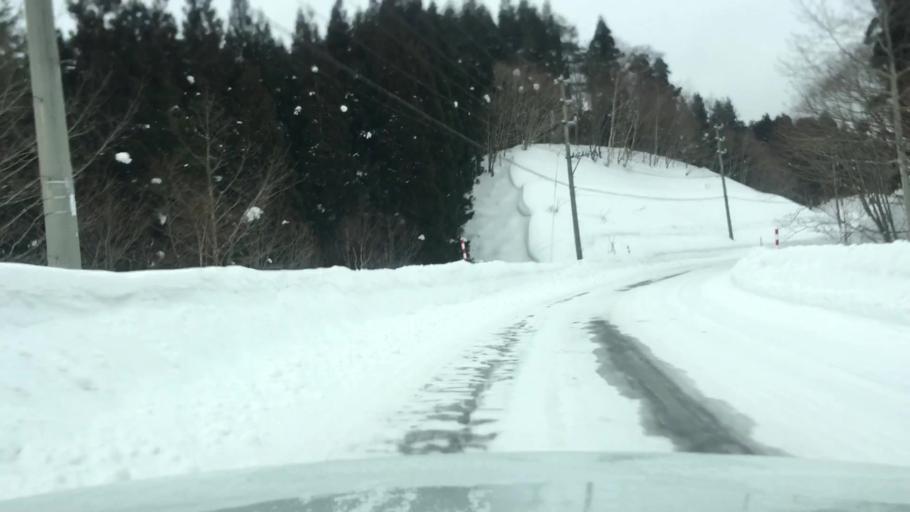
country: JP
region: Akita
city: Hanawa
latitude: 39.9953
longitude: 140.9916
